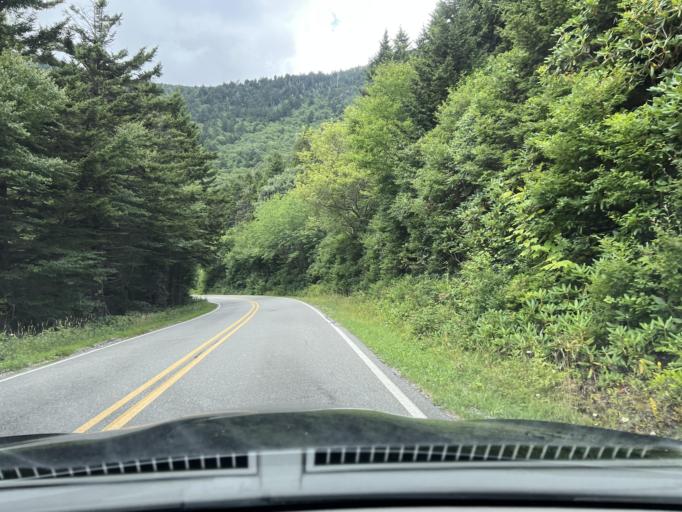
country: US
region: North Carolina
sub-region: Buncombe County
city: Black Mountain
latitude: 35.7295
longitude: -82.2816
